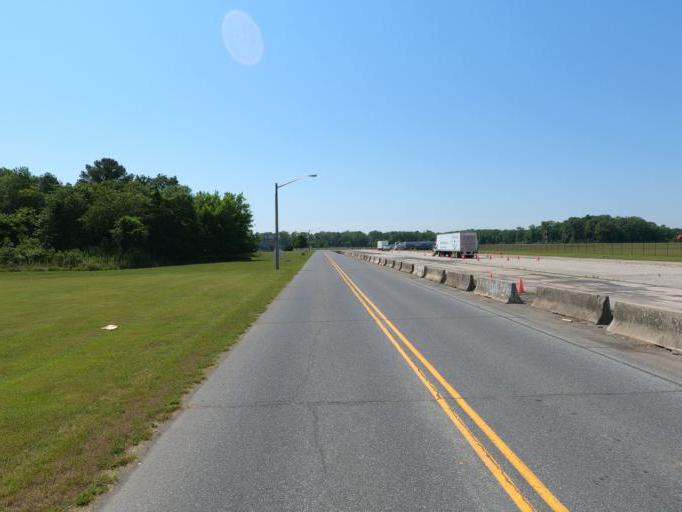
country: US
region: Delaware
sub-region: Sussex County
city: Georgetown
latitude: 38.6883
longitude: -75.3519
